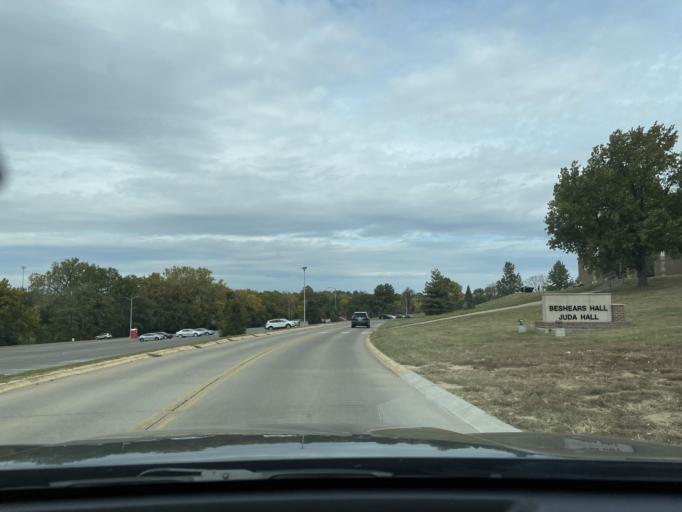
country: US
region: Missouri
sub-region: Buchanan County
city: Saint Joseph
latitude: 39.7594
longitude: -94.7830
